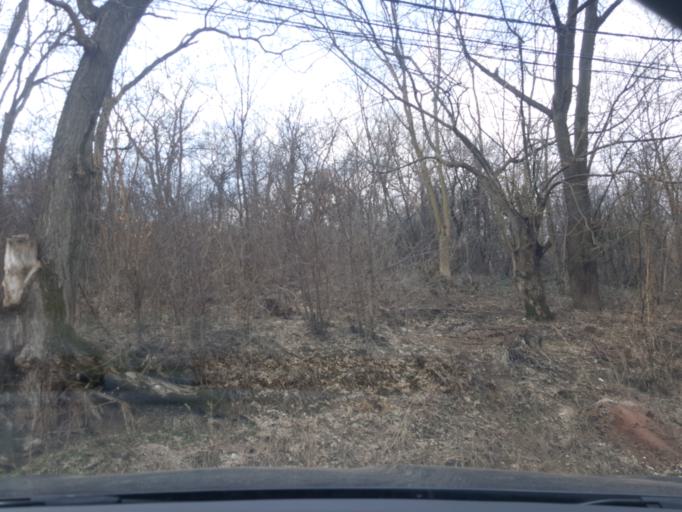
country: RS
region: Central Serbia
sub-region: Nisavski Okrug
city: Nis
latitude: 43.3116
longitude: 21.8664
